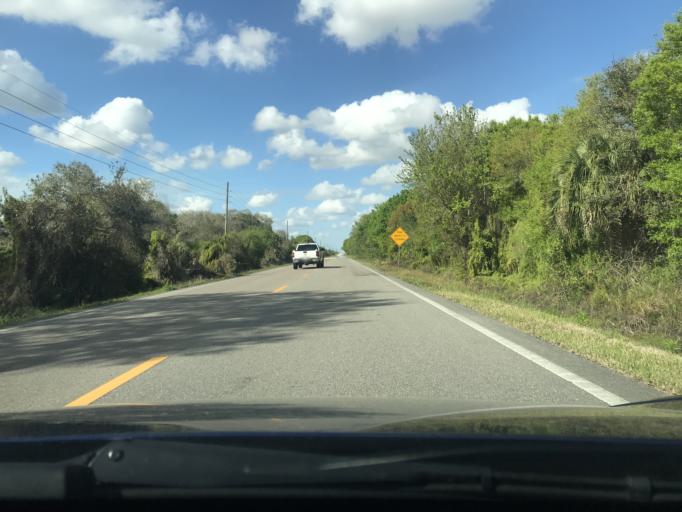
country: US
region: Florida
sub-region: Okeechobee County
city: Taylor Creek
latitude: 27.2245
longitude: -80.6943
